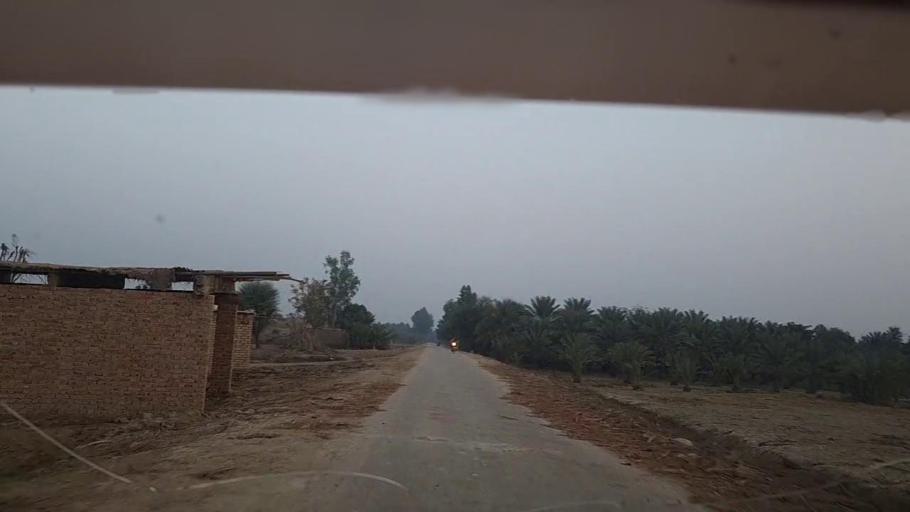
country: PK
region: Sindh
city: Khairpur
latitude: 27.5760
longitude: 68.7212
